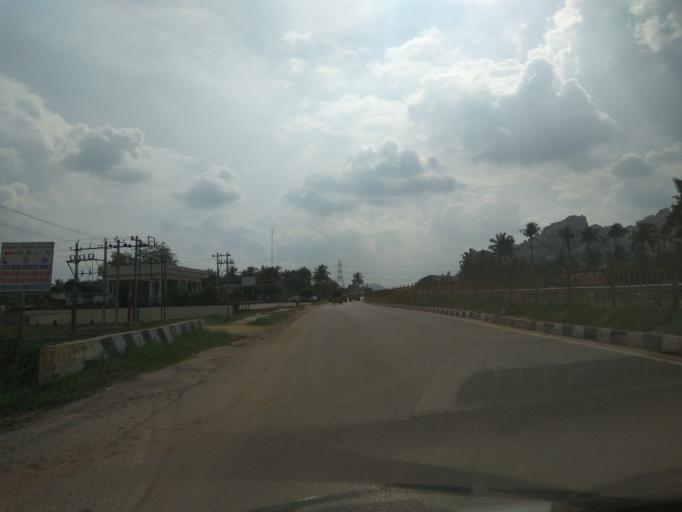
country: IN
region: Karnataka
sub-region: Kolar
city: Kolar
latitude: 13.1235
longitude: 78.1083
